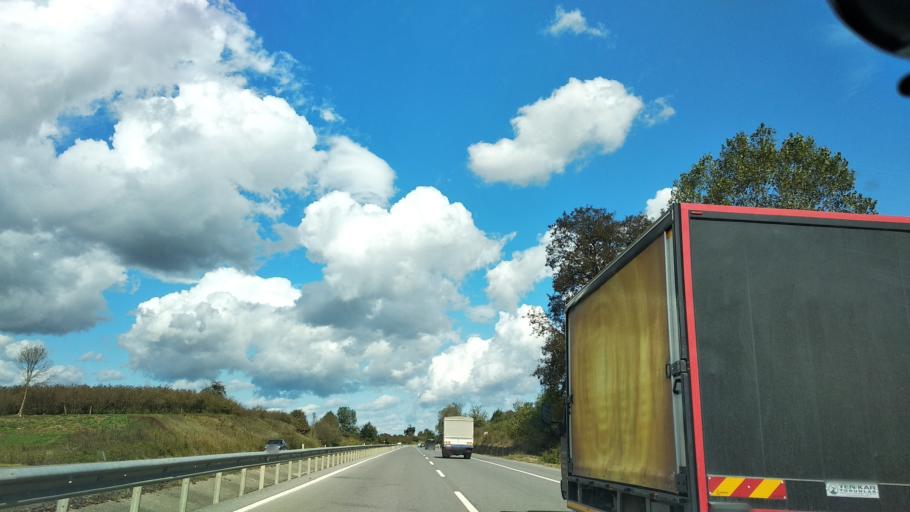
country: TR
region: Sakarya
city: Ferizli
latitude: 40.9748
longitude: 30.5133
